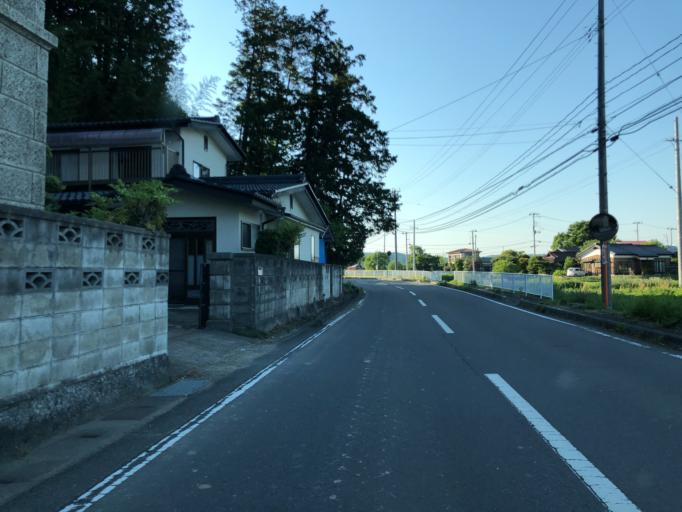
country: JP
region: Fukushima
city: Ishikawa
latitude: 36.9525
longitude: 140.4360
